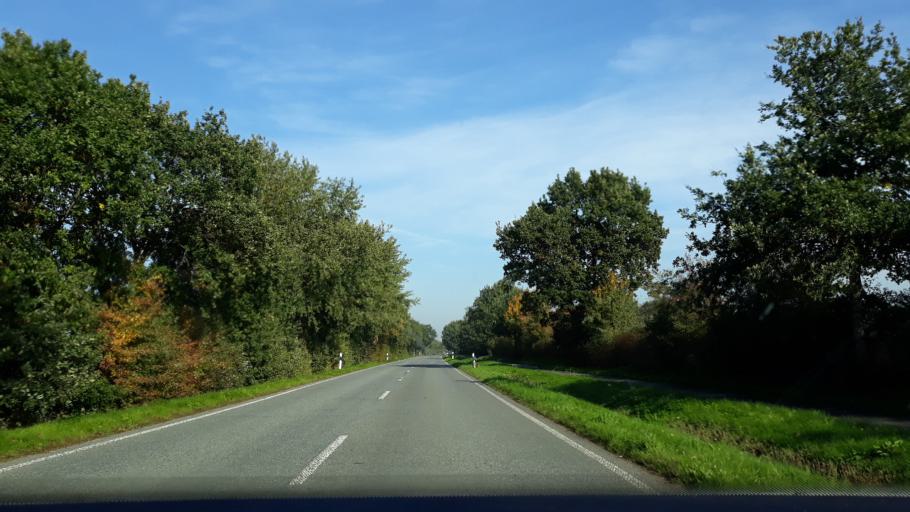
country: DE
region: Schleswig-Holstein
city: Gross Rheide
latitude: 54.4315
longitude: 9.4165
